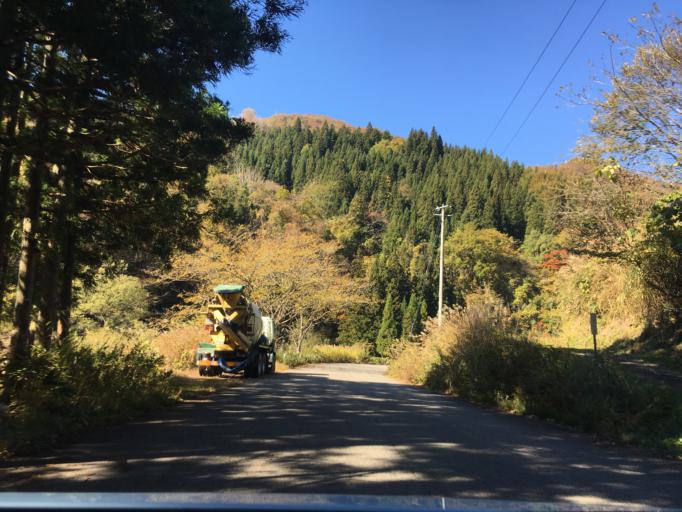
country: JP
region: Fukushima
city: Inawashiro
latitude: 37.4155
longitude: 139.9906
